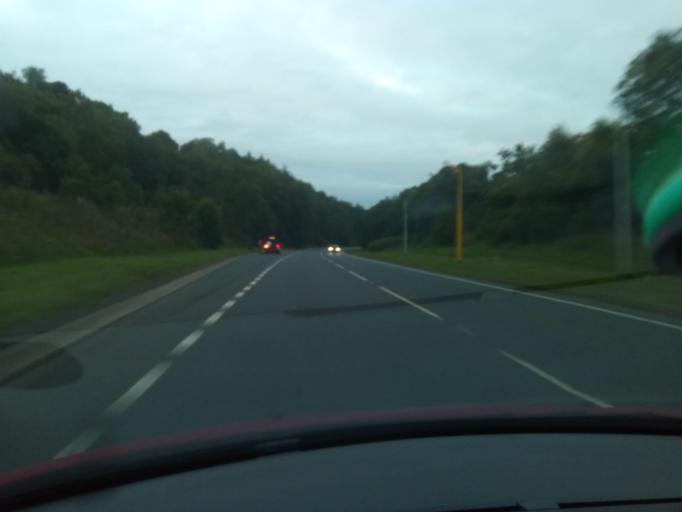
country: GB
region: England
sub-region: Northumberland
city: Bardon Mill
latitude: 54.9748
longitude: -2.2938
